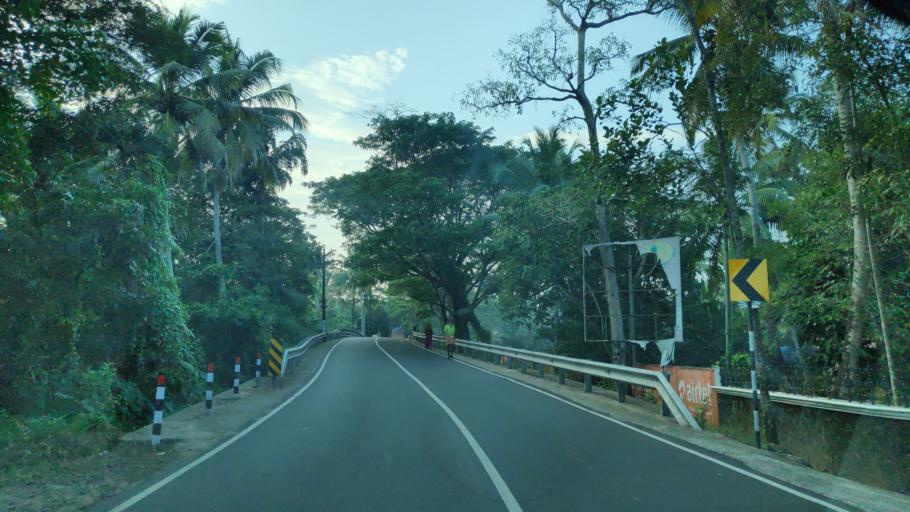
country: IN
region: Kerala
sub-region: Alappuzha
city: Shertallai
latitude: 9.6774
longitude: 76.3789
